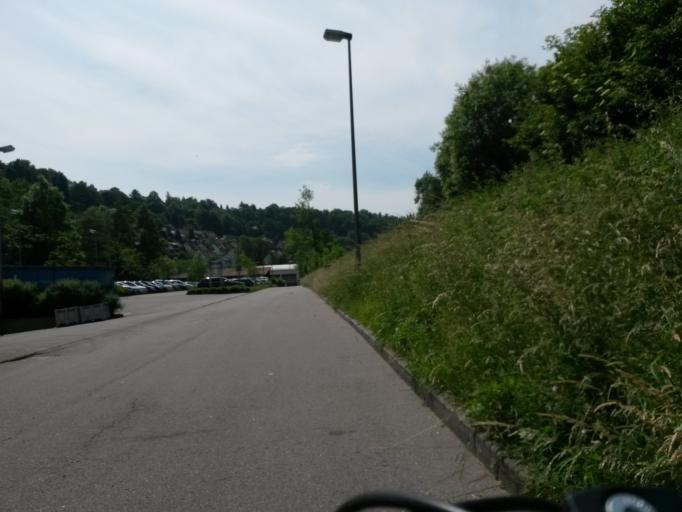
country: DE
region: Baden-Wuerttemberg
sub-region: Karlsruhe Region
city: Wildberg
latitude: 48.6342
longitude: 8.7464
